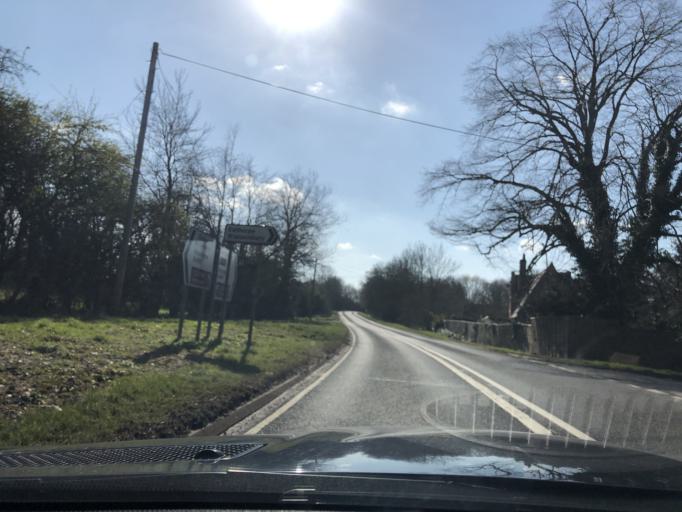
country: GB
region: England
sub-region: Warwickshire
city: Long Itchington
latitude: 52.3191
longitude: -1.4239
